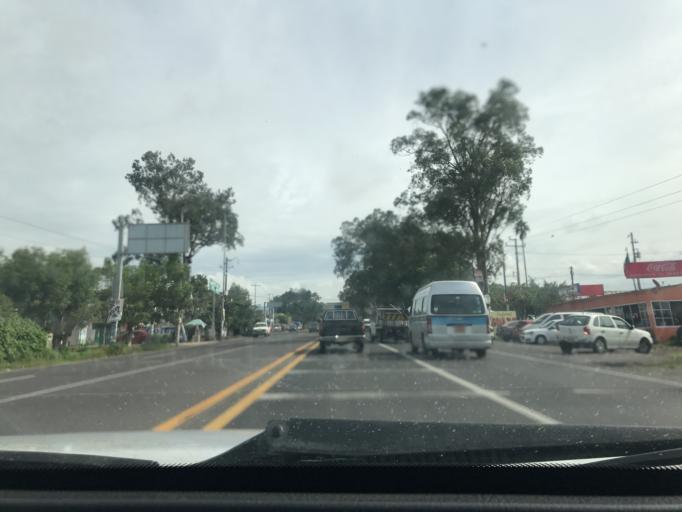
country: MX
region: Morelos
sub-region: Atlatlahucan
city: Colonia San Francisco
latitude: 18.8970
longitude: -98.9088
